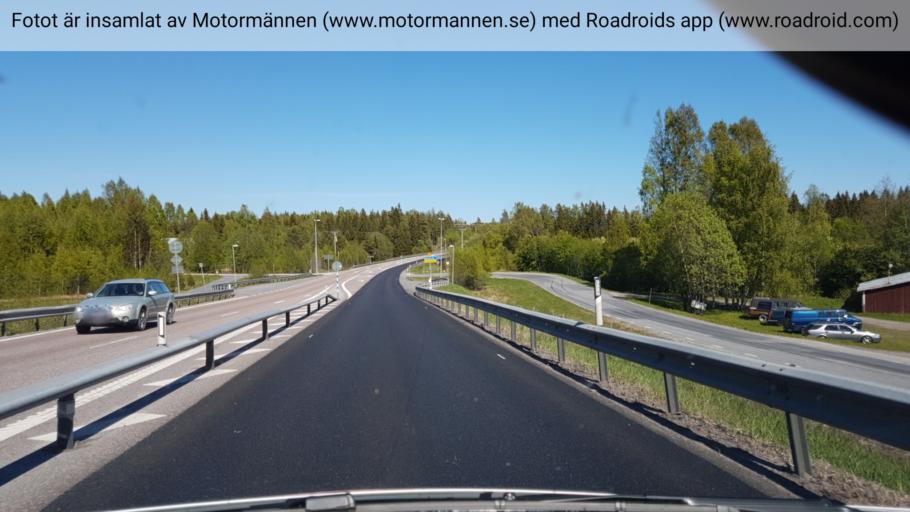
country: SE
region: Vaesternorrland
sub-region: OErnskoeldsviks Kommun
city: Husum
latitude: 63.3411
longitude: 19.1116
